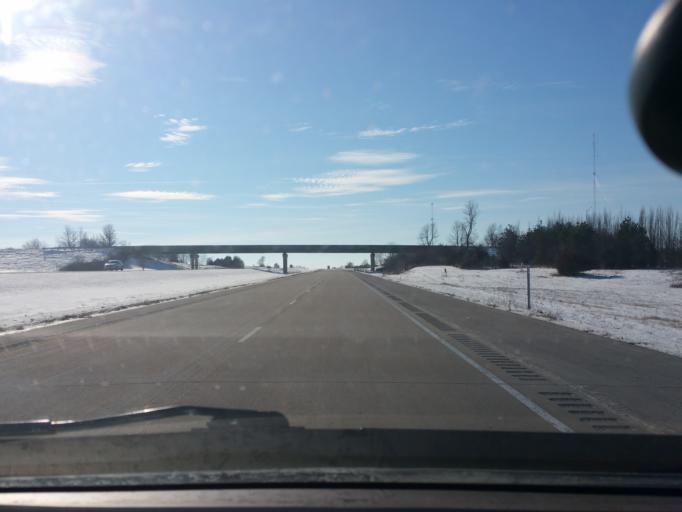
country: US
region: Iowa
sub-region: Decatur County
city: Leon
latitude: 40.8722
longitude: -93.8025
